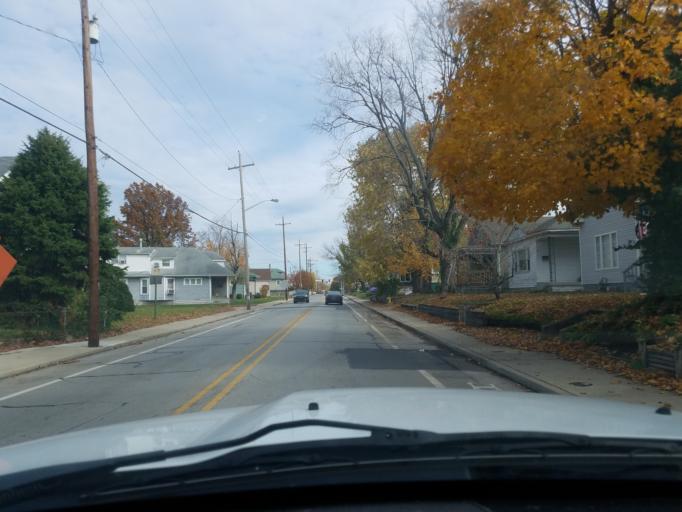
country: US
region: Indiana
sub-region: Floyd County
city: New Albany
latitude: 38.3024
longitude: -85.8147
